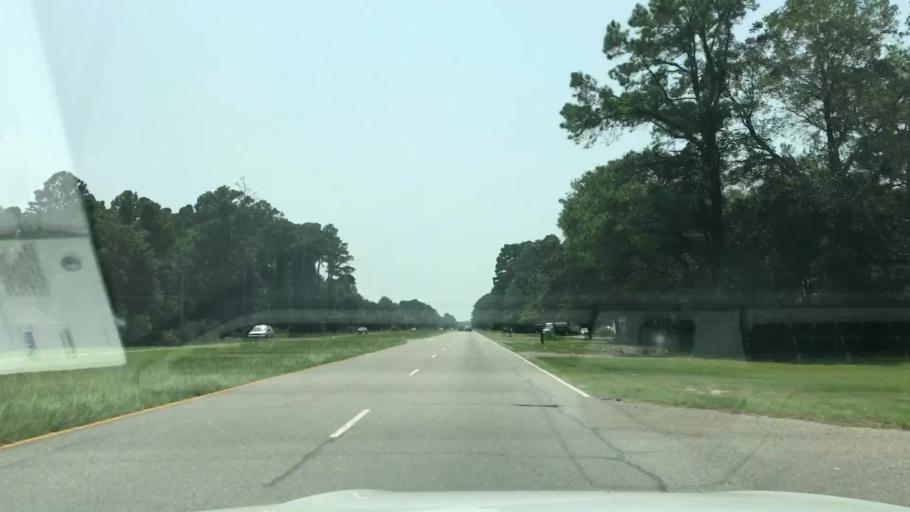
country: US
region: South Carolina
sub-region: Georgetown County
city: Georgetown
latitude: 33.3141
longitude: -79.3284
